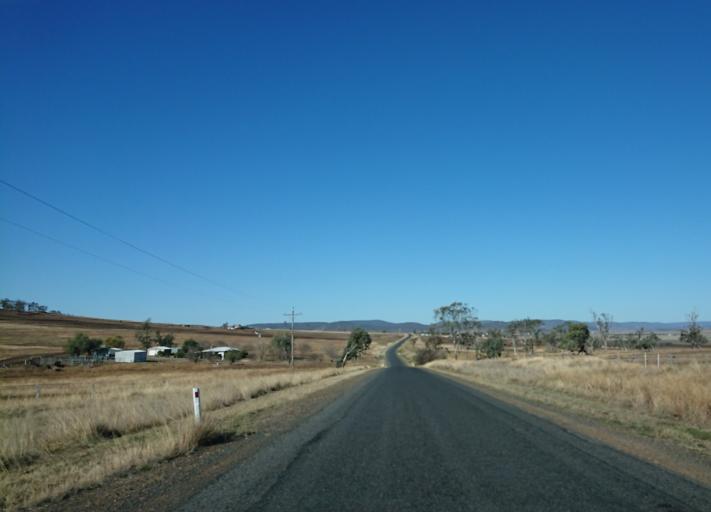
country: AU
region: Queensland
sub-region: Toowoomba
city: Top Camp
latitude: -27.8091
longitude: 151.9546
